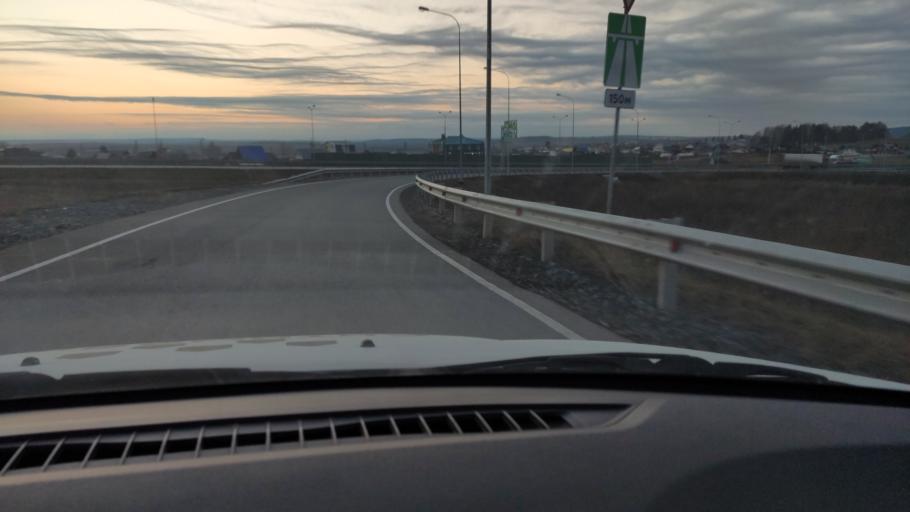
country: RU
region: Perm
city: Lobanovo
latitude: 57.8026
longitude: 56.3272
